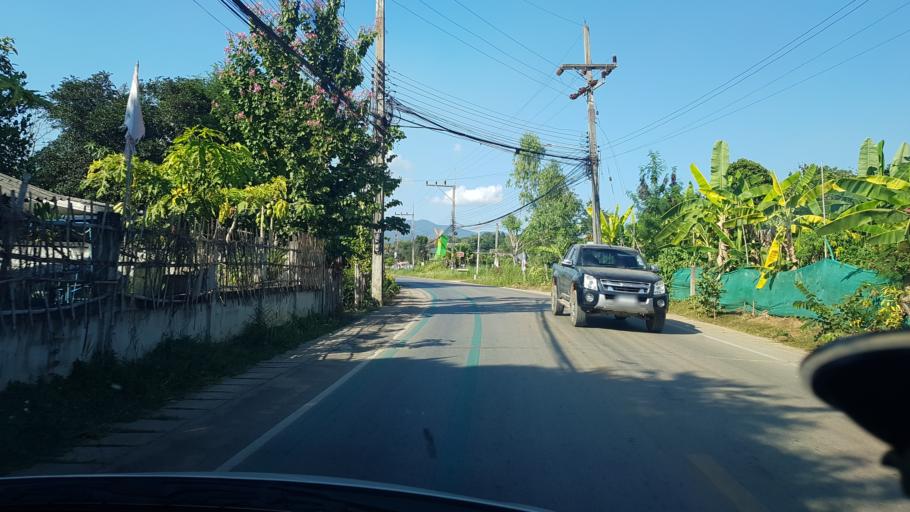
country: TH
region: Chiang Rai
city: Chiang Rai
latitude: 19.9461
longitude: 99.8104
